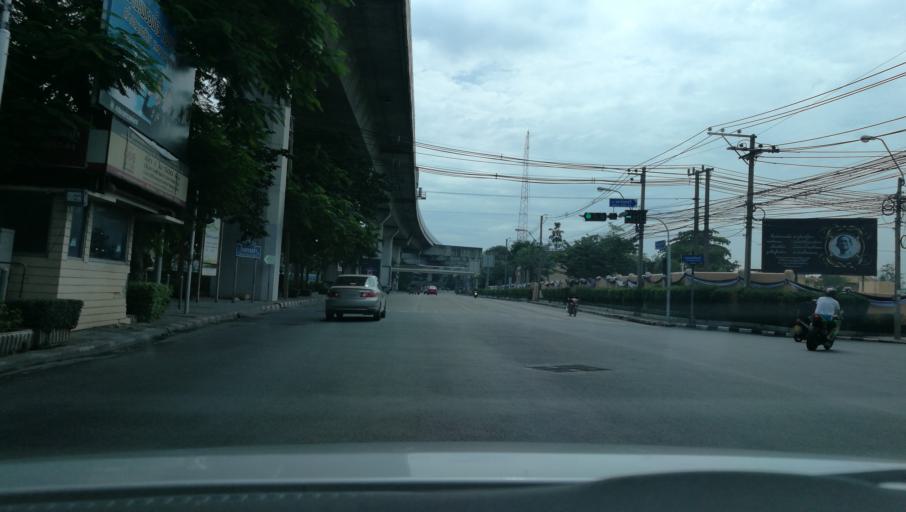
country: TH
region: Bangkok
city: Dusit
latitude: 13.7752
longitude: 100.5312
